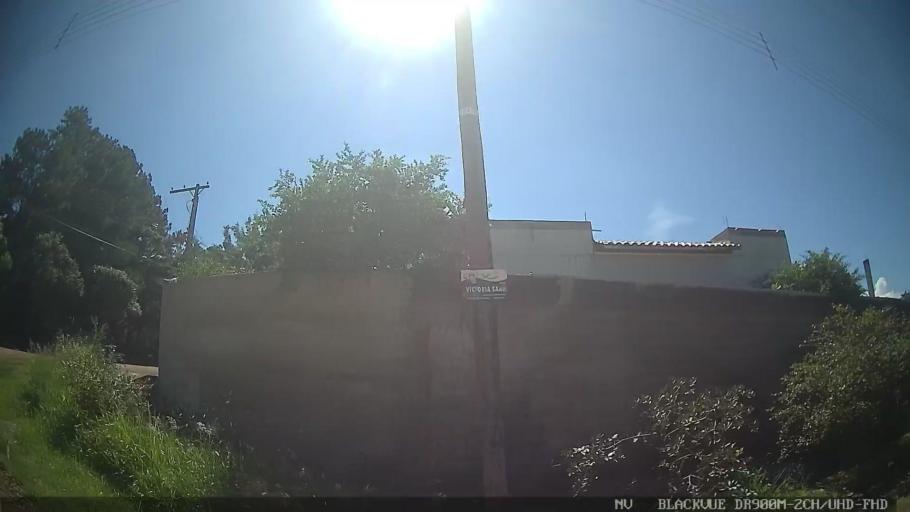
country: BR
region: Sao Paulo
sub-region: Atibaia
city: Atibaia
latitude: -23.1025
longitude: -46.5767
